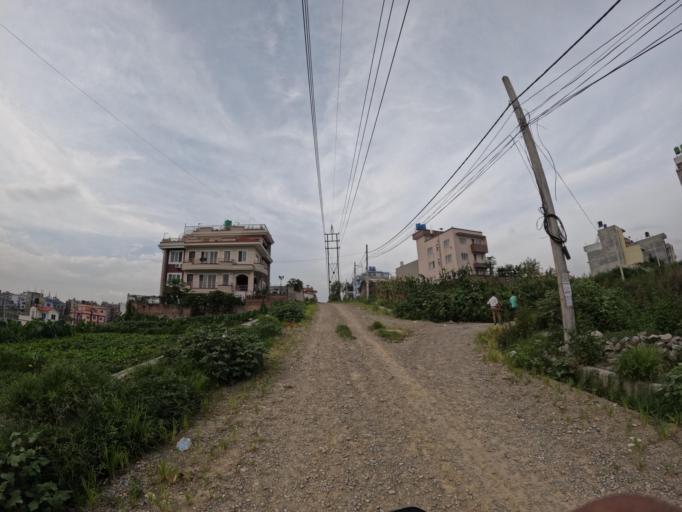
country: NP
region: Central Region
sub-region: Bagmati Zone
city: Bhaktapur
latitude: 27.6796
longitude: 85.3907
